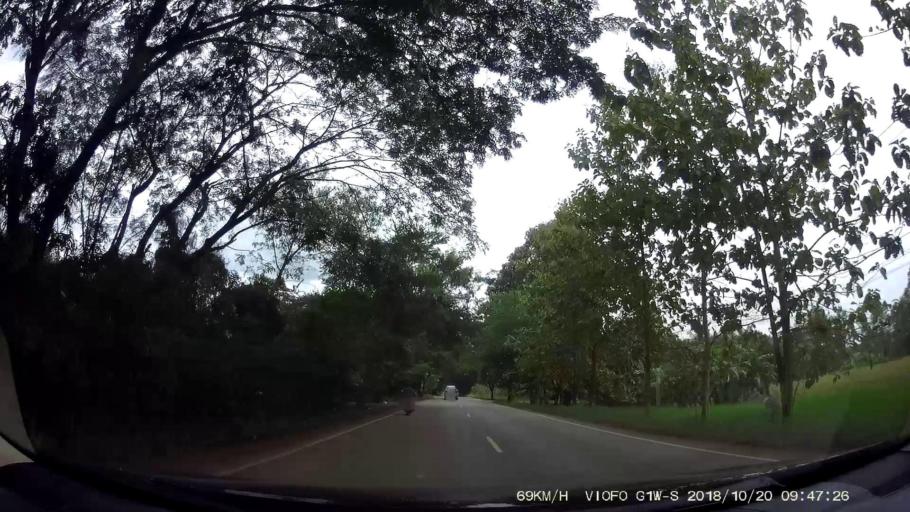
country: TH
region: Chaiyaphum
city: Khon San
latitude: 16.5036
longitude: 101.9196
